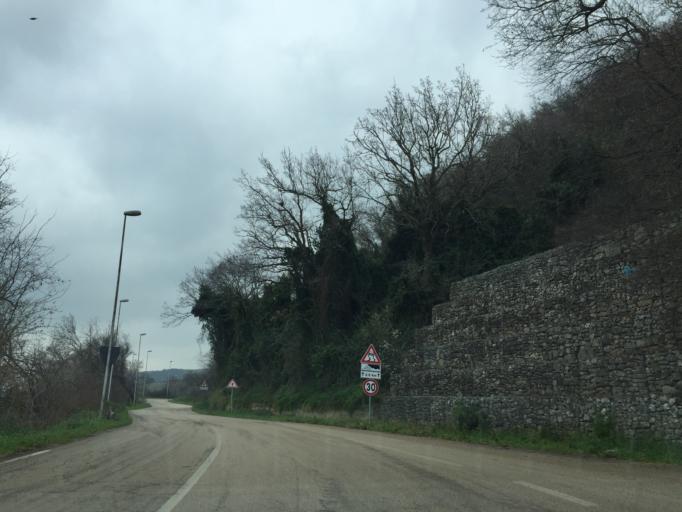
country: IT
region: Apulia
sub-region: Provincia di Foggia
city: Bovino
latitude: 41.2731
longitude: 15.3668
